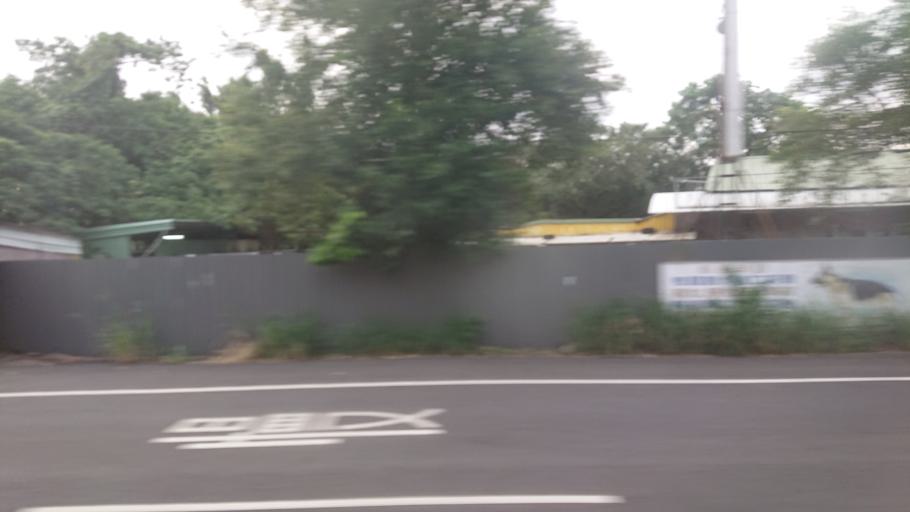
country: TW
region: Taiwan
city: Daxi
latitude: 24.8795
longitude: 121.2597
